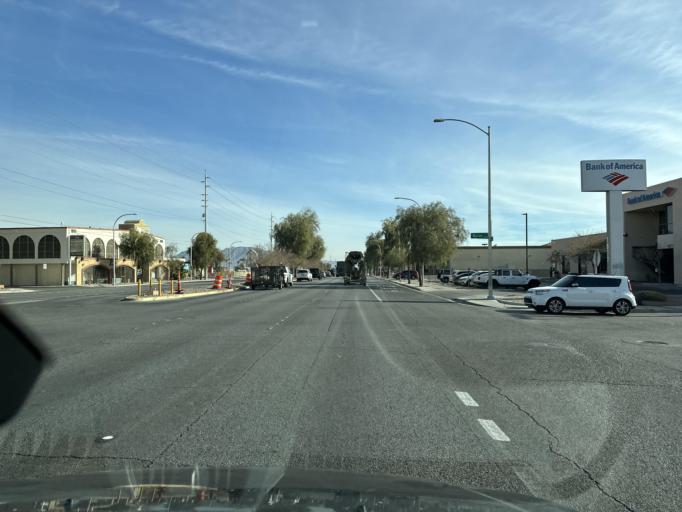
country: US
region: Nevada
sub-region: Clark County
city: Winchester
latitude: 36.1440
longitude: -115.1404
